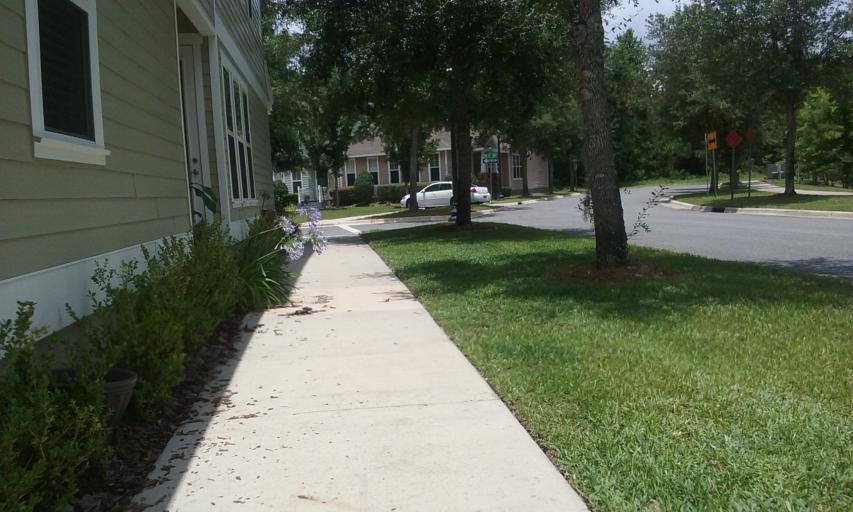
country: US
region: Florida
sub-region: Alachua County
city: Gainesville
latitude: 29.6835
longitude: -82.3575
